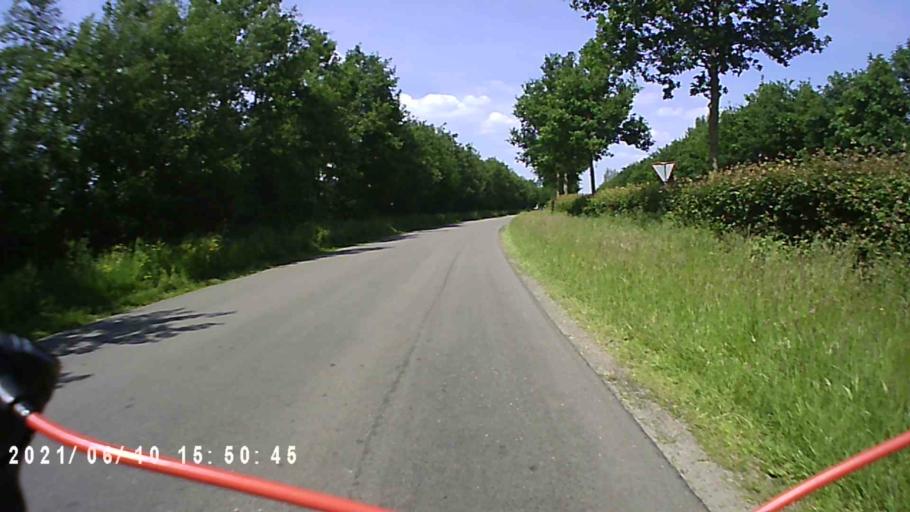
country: NL
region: Friesland
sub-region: Gemeente Achtkarspelen
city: Harkema
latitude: 53.1704
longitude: 6.1183
